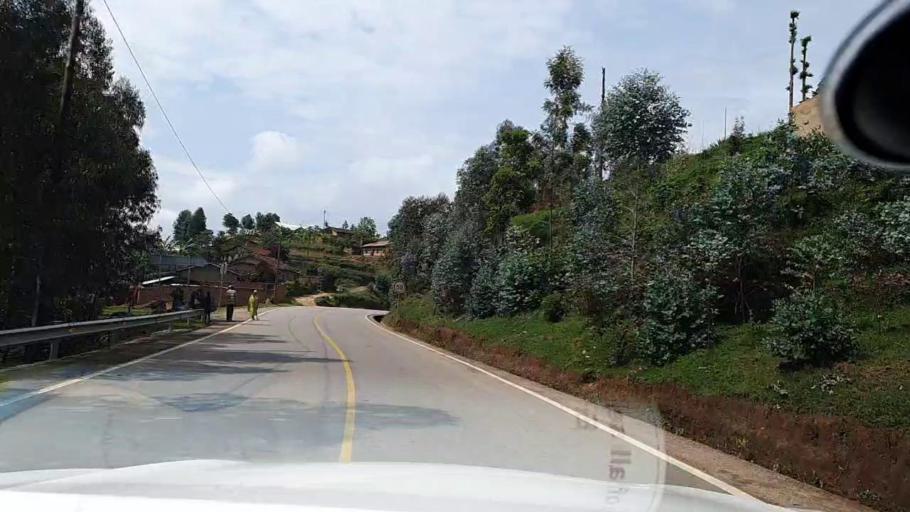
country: RW
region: Southern Province
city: Nzega
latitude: -2.4836
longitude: 29.5197
